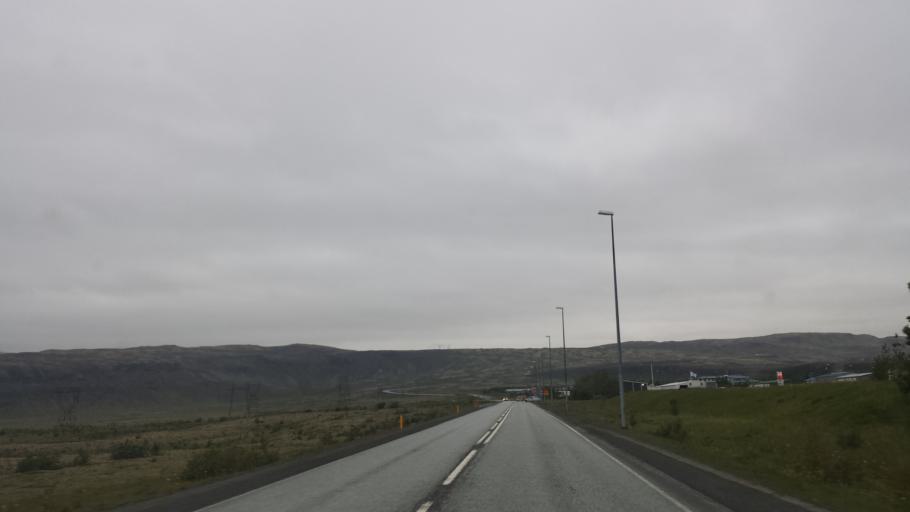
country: IS
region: South
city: Hveragerdi
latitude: 63.9920
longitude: -21.1812
